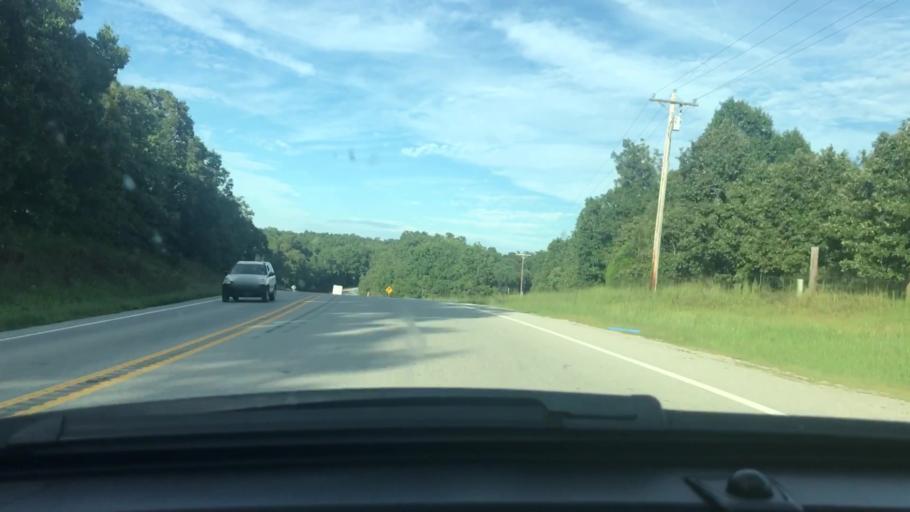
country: US
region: Arkansas
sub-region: Sharp County
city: Cherokee Village
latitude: 36.2743
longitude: -91.3177
